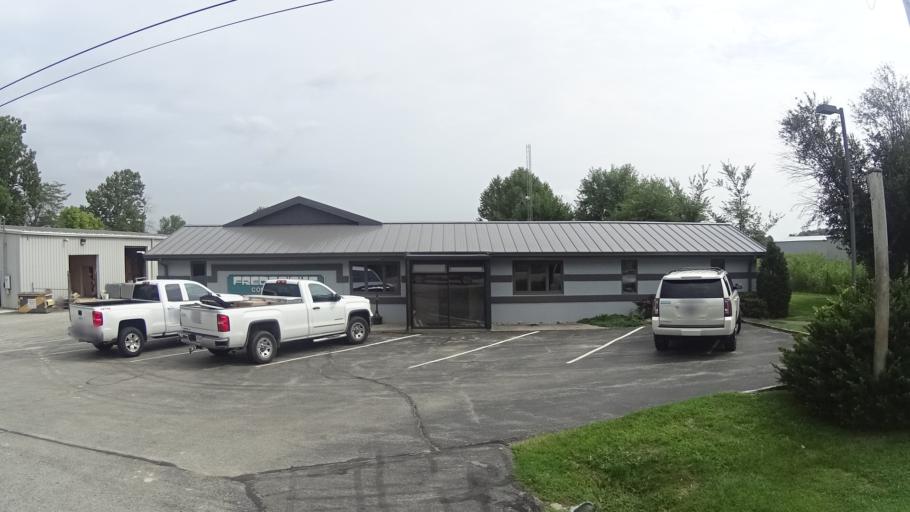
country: US
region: Indiana
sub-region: Madison County
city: Pendleton
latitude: 40.0238
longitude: -85.7763
